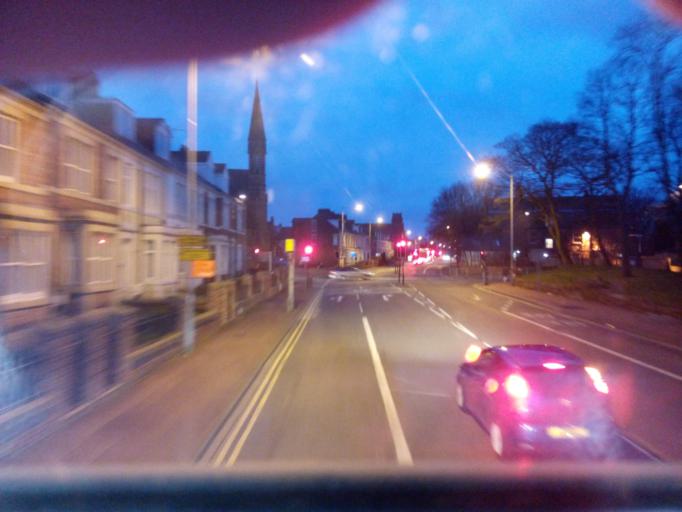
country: GB
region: England
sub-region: Gateshead
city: Gateshead
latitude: 54.9520
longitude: -1.5992
